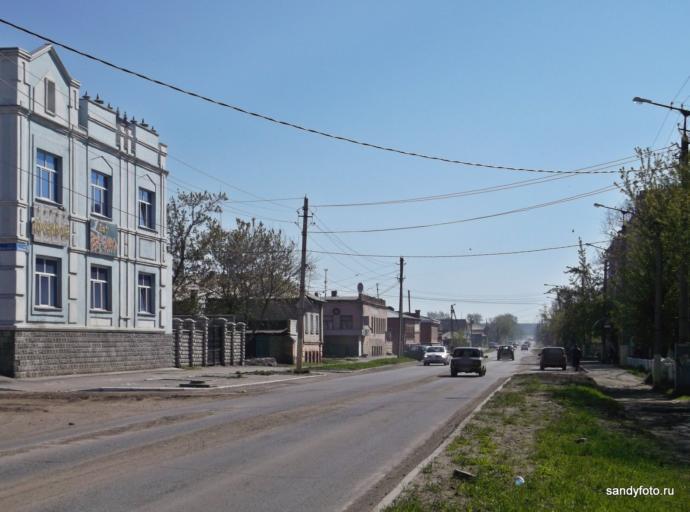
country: RU
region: Chelyabinsk
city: Troitsk
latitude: 54.0949
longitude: 61.5746
